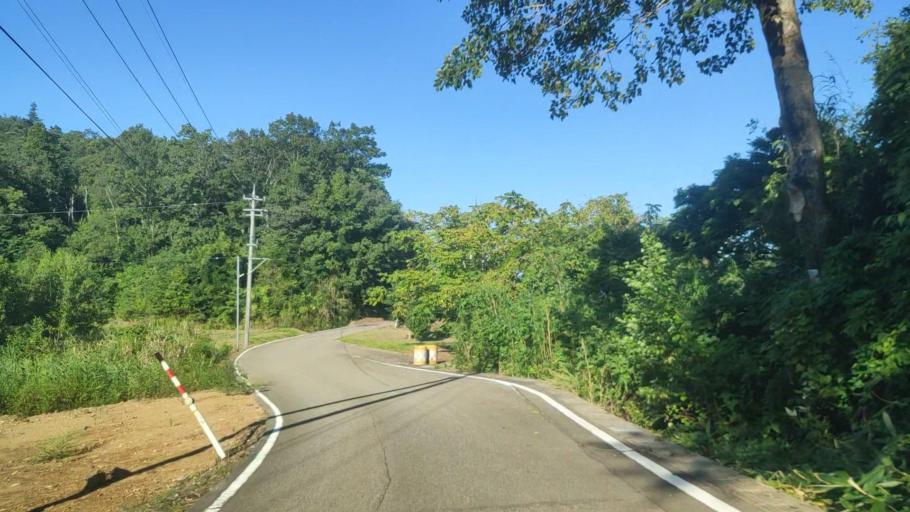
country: JP
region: Ishikawa
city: Nanao
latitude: 37.1183
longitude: 136.8925
